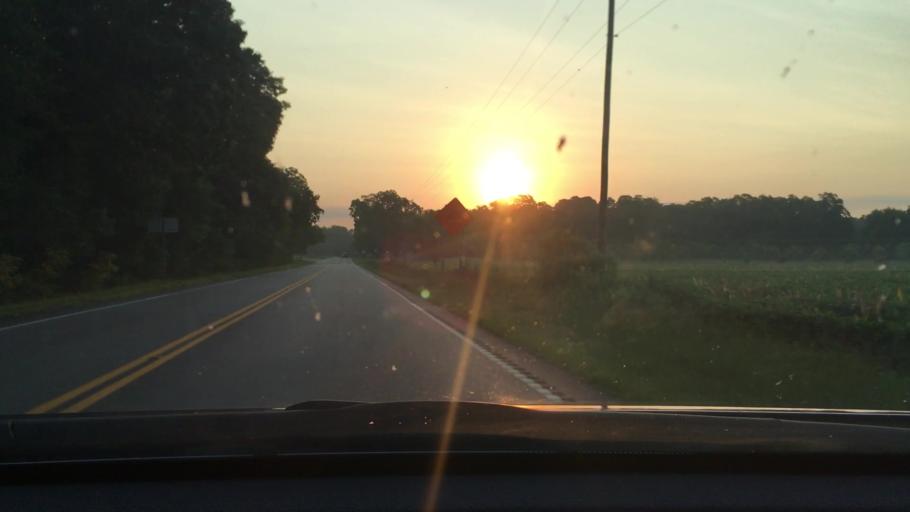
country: US
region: South Carolina
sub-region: Darlington County
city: Hartsville
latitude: 34.2693
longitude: -80.1363
